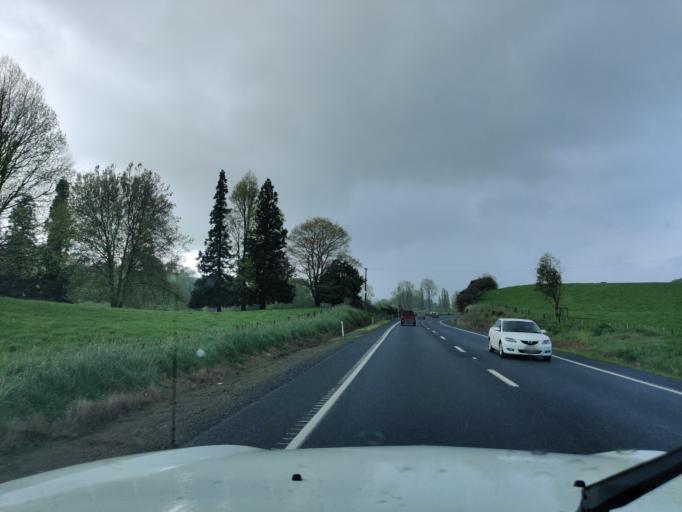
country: NZ
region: Waikato
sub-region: Matamata-Piako District
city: Matamata
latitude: -37.9789
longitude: 175.7006
